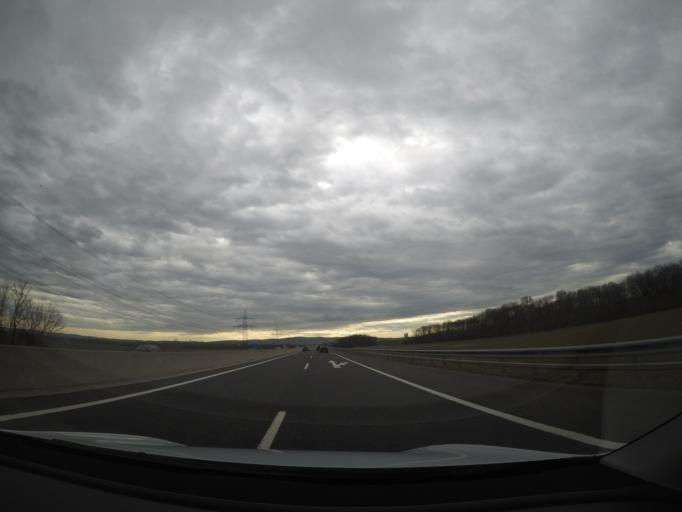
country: AT
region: Lower Austria
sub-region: Politischer Bezirk Baden
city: Ebreichsdorf
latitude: 47.9328
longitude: 16.3851
